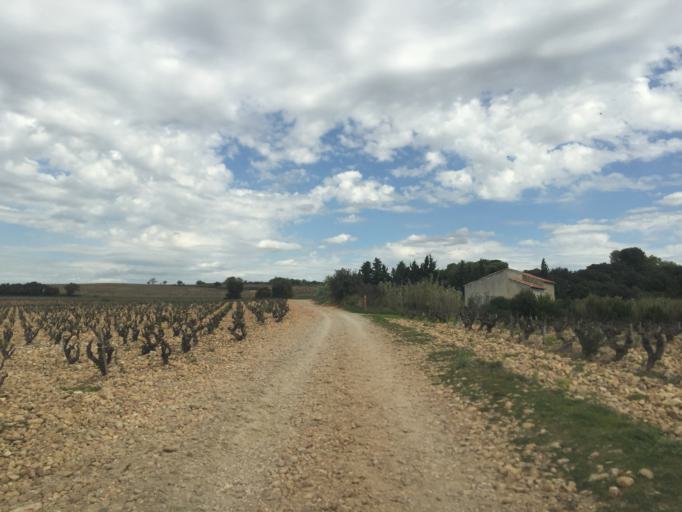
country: FR
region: Provence-Alpes-Cote d'Azur
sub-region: Departement du Vaucluse
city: Bedarrides
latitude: 44.0361
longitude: 4.8760
